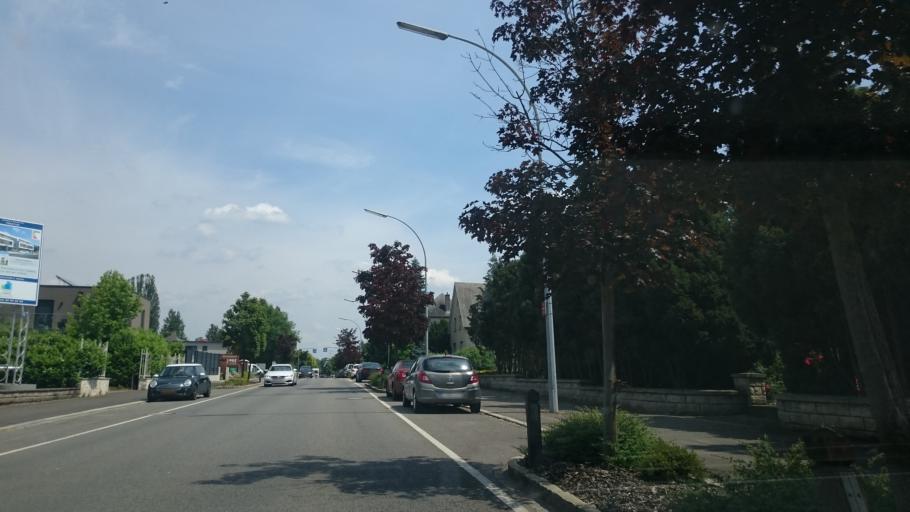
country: LU
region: Luxembourg
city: Capellen
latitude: 49.6462
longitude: 5.9751
